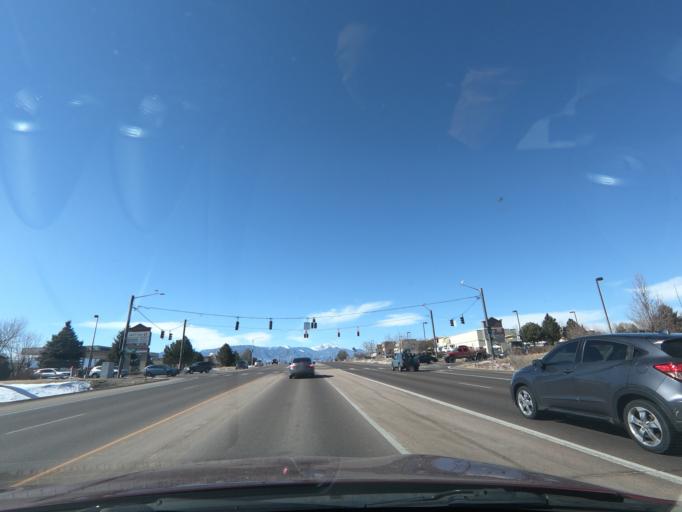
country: US
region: Colorado
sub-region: El Paso County
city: Security-Widefield
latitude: 38.7180
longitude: -104.6972
